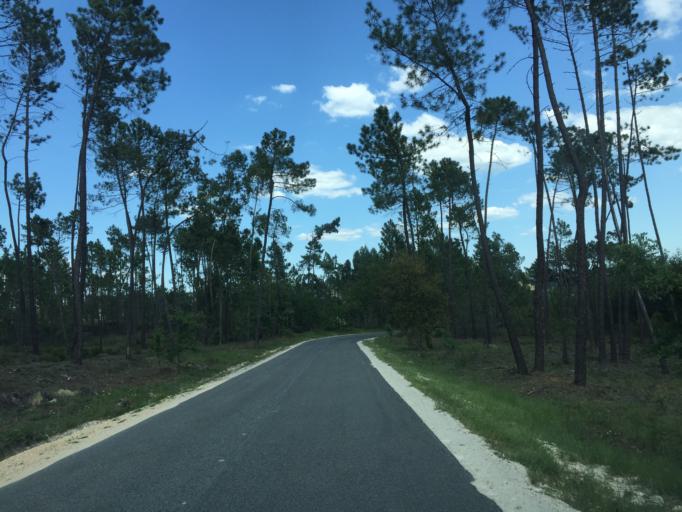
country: PT
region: Leiria
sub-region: Alvaiazere
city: Alvaiazere
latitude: 39.7527
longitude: -8.4698
